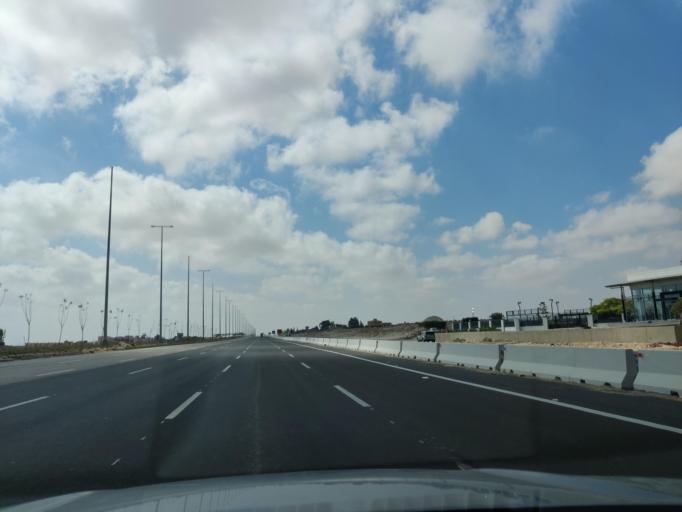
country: EG
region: Muhafazat Matruh
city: Al `Alamayn
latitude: 30.9355
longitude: 28.7875
